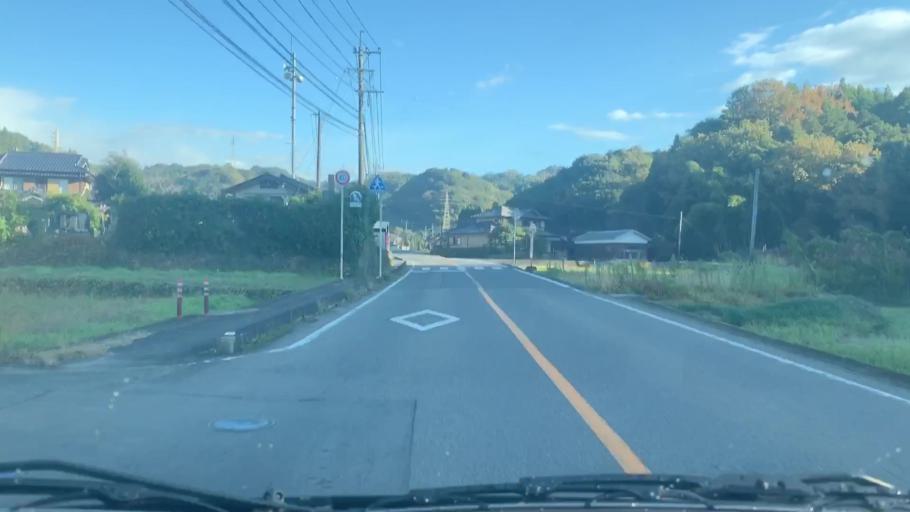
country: JP
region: Saga Prefecture
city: Takeocho-takeo
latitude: 33.2317
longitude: 130.0607
